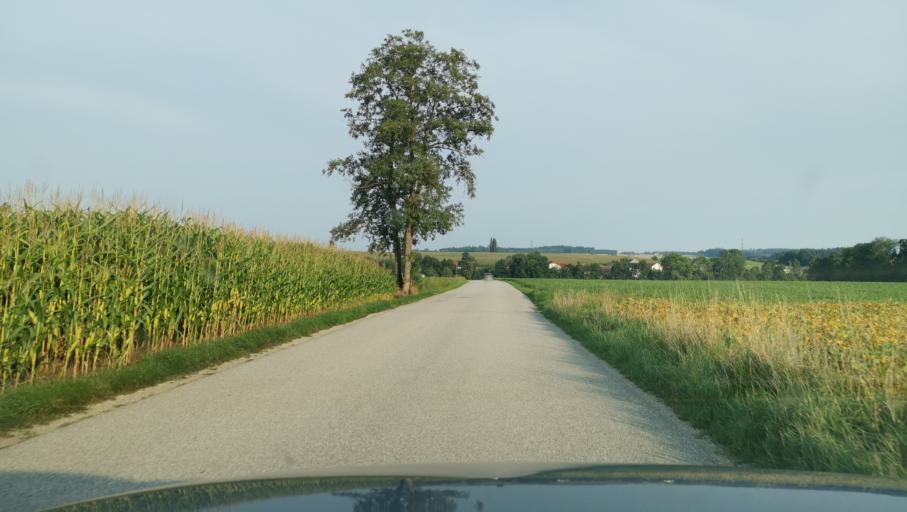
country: AT
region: Upper Austria
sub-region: Politischer Bezirk Grieskirchen
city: Grieskirchen
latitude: 48.2904
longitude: 13.8044
